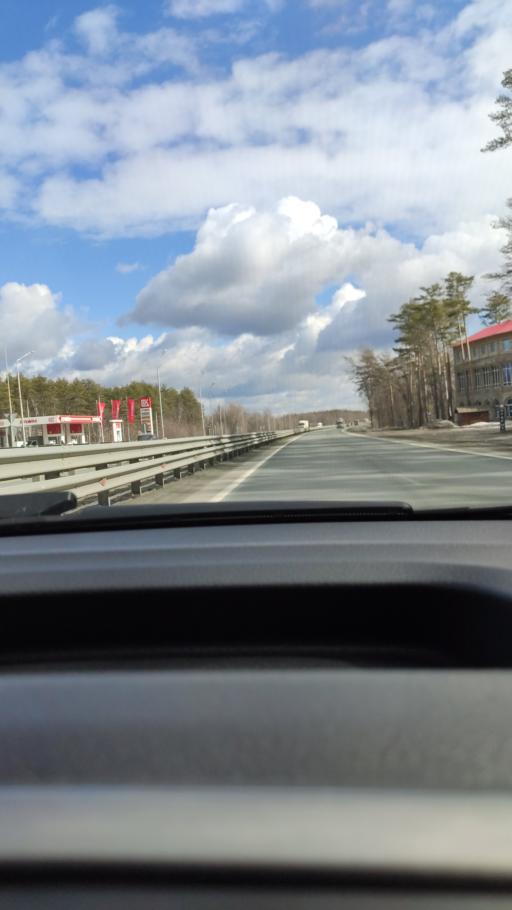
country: RU
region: Samara
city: Zhigulevsk
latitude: 53.5123
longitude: 49.5730
